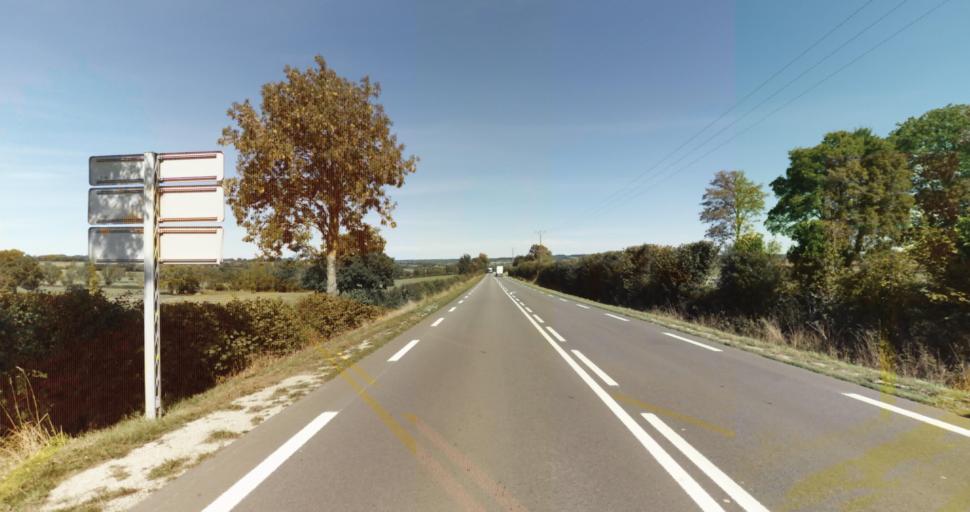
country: FR
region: Lower Normandy
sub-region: Departement de l'Orne
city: Gace
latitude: 48.7476
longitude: 0.2709
